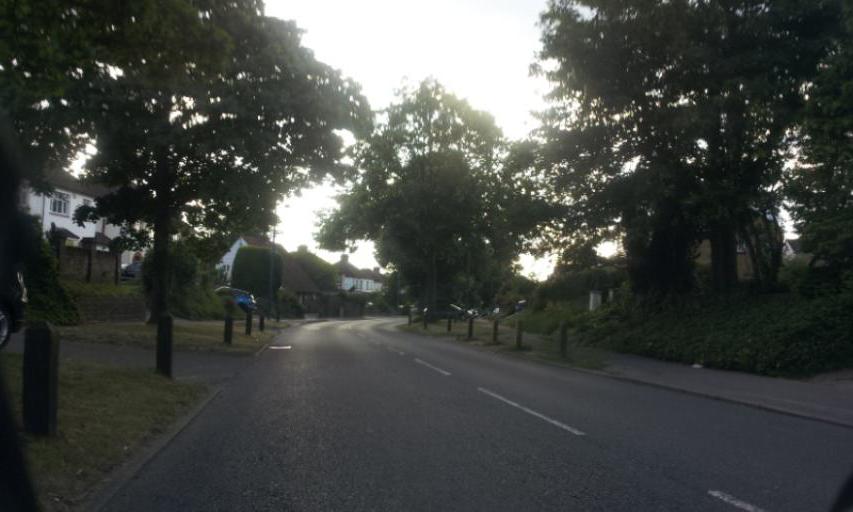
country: GB
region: England
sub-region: Kent
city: Boxley
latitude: 51.2889
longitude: 0.5348
